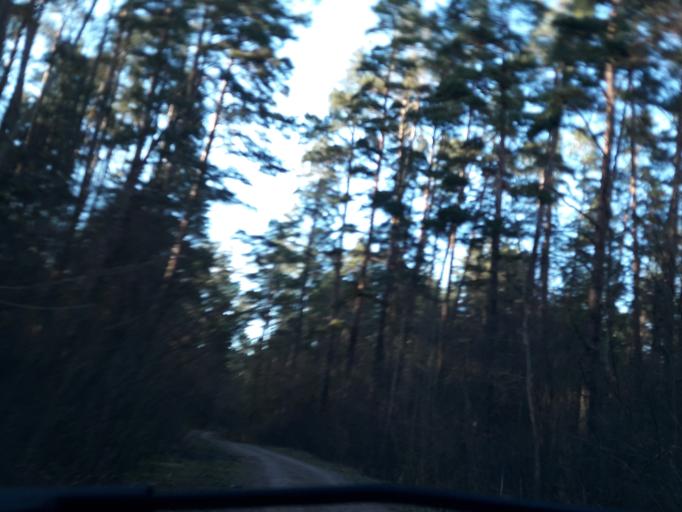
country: LV
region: Kekava
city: Kekava
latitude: 56.8567
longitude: 24.2320
